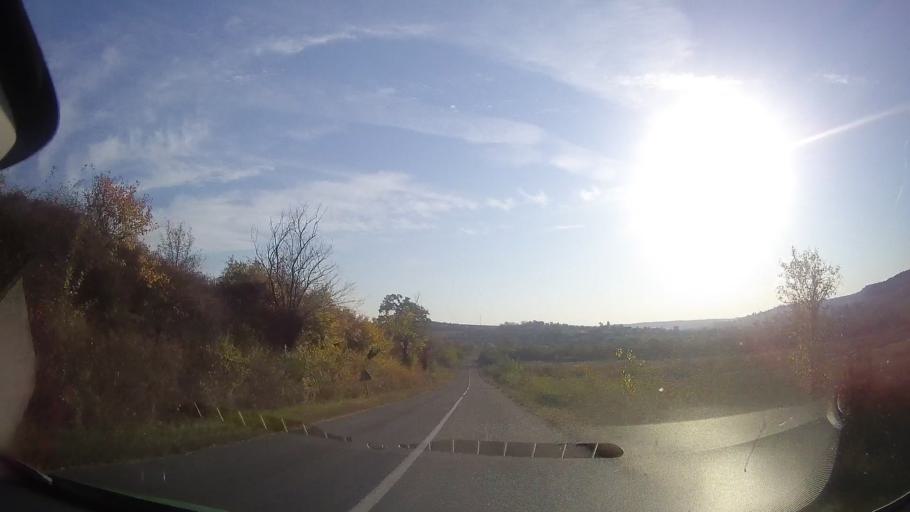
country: RO
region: Timis
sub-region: Comuna Bogda
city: Bogda
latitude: 45.9811
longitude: 21.5654
